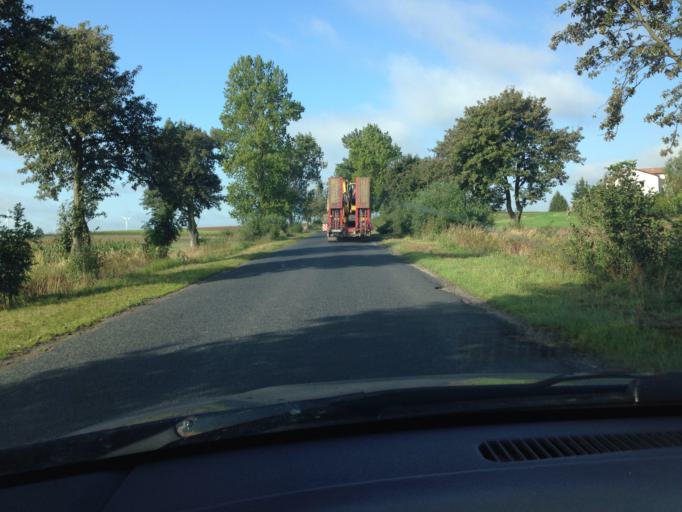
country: PL
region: Kujawsko-Pomorskie
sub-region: Powiat rypinski
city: Rypin
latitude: 53.1060
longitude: 19.4671
